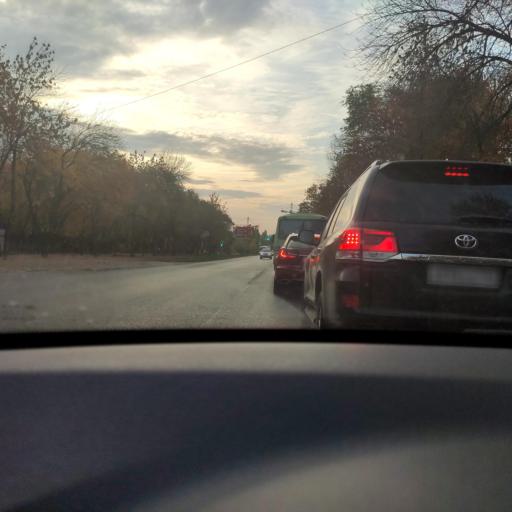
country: RU
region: Samara
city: Samara
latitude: 53.2156
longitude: 50.2103
